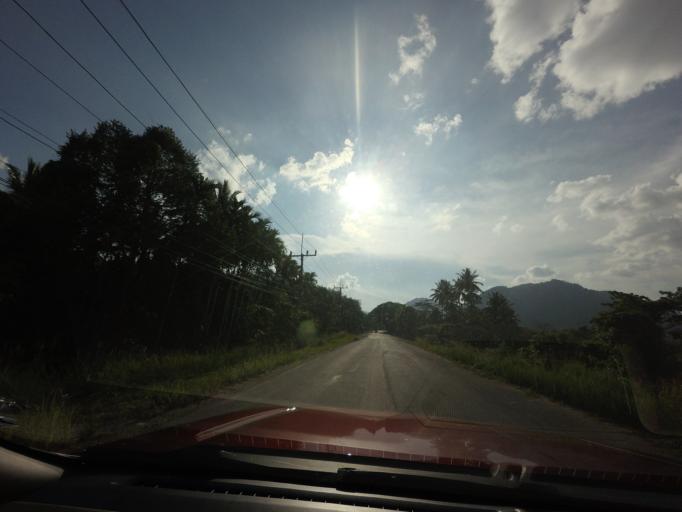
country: TH
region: Yala
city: Ban Nang Sata
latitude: 6.2233
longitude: 101.2258
